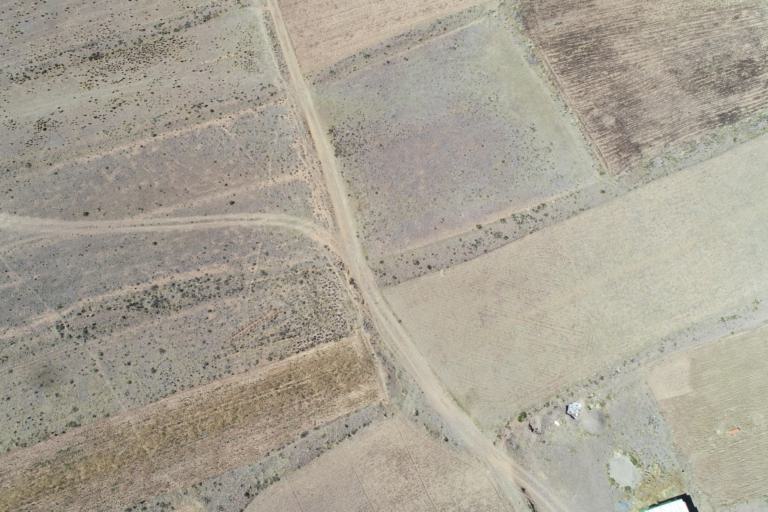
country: BO
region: La Paz
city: Achacachi
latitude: -15.9000
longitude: -68.8997
